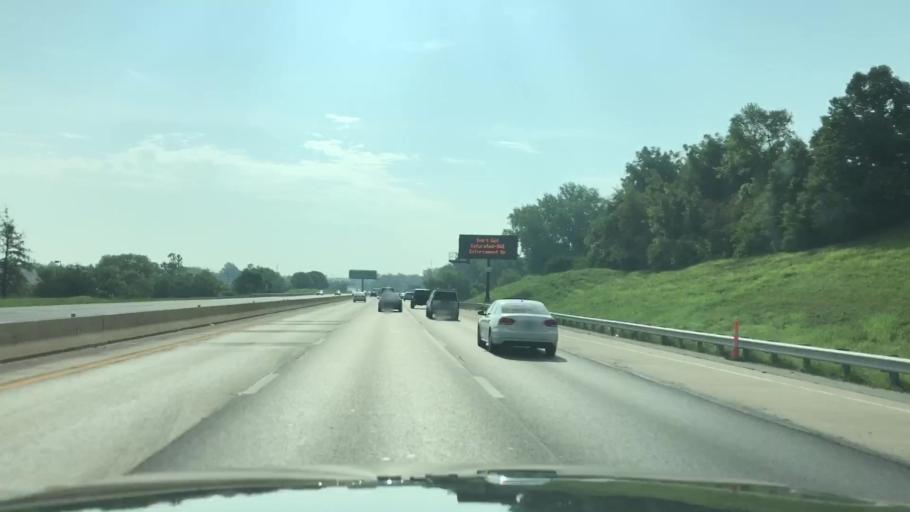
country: US
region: Missouri
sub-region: Saint Louis County
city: Bridgeton
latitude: 38.7450
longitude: -90.4269
